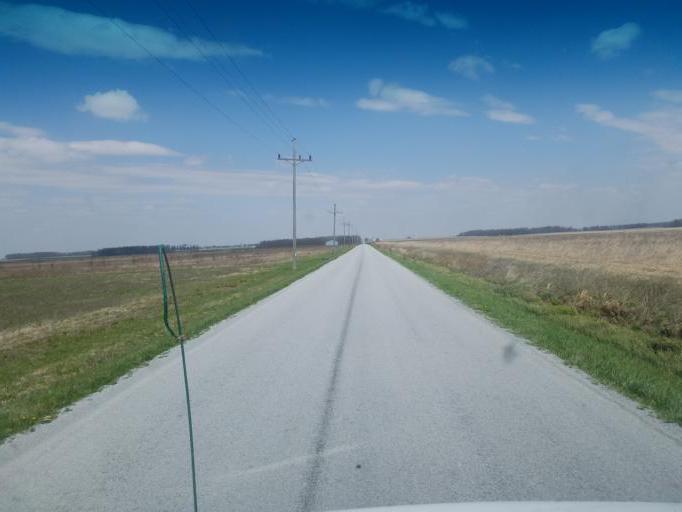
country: US
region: Ohio
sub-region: Hardin County
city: Forest
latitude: 40.7628
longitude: -83.4965
